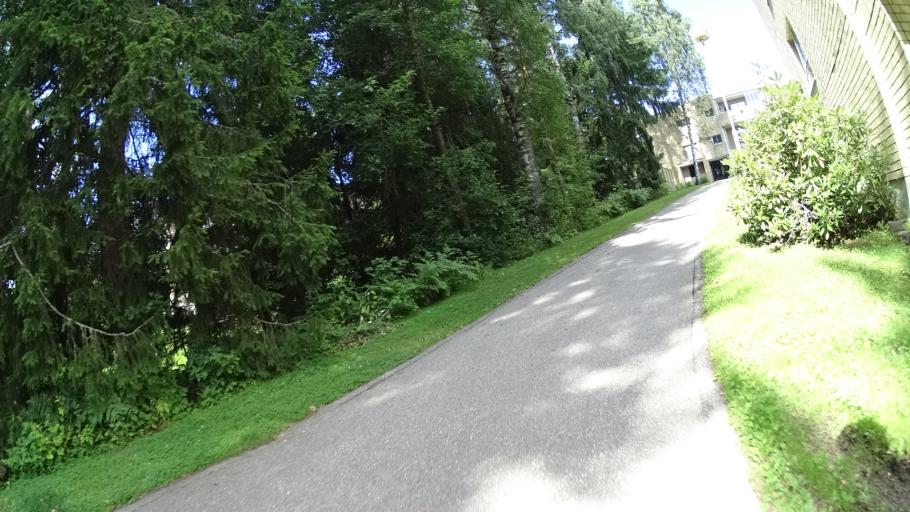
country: FI
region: Uusimaa
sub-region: Helsinki
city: Kauniainen
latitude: 60.2118
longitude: 24.7234
